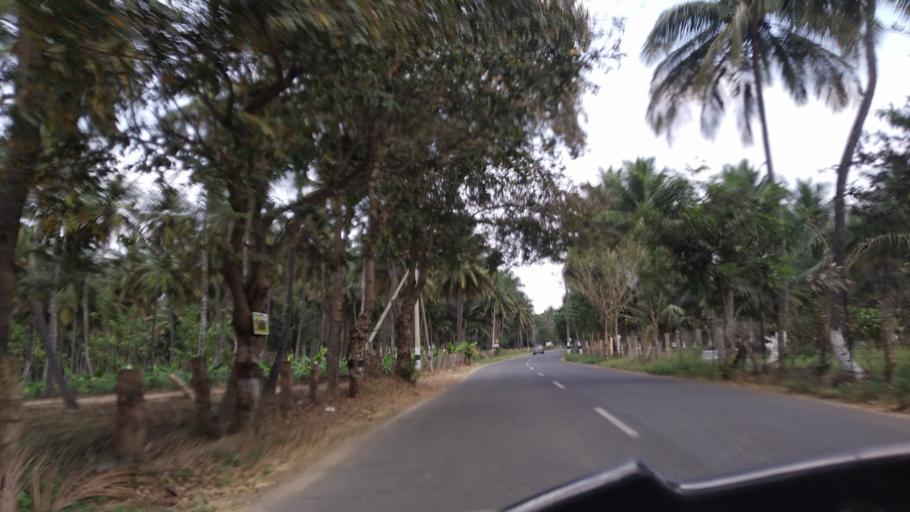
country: IN
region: Tamil Nadu
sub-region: Coimbatore
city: Perur
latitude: 10.9588
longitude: 76.7511
